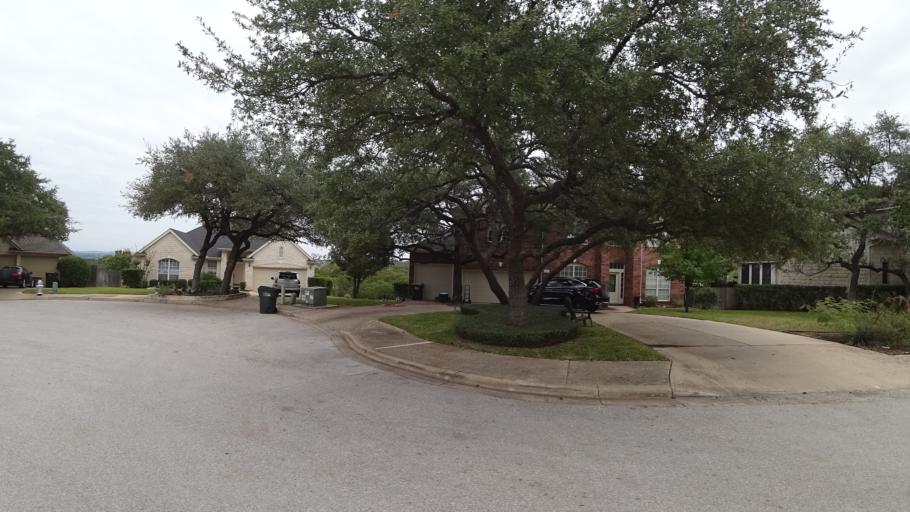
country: US
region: Texas
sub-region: Travis County
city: Bee Cave
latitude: 30.3104
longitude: -97.9281
